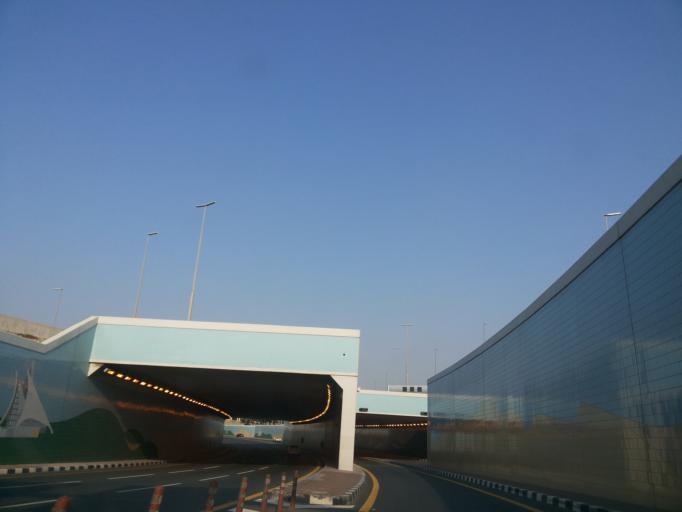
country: AE
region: Ash Shariqah
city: Sharjah
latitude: 25.2323
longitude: 55.3023
